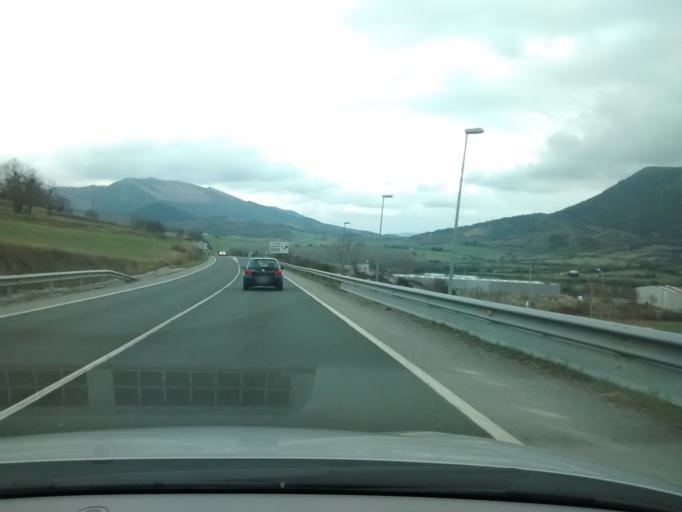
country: ES
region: Basque Country
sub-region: Bizkaia
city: Balmaseda
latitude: 43.1616
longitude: -3.2416
